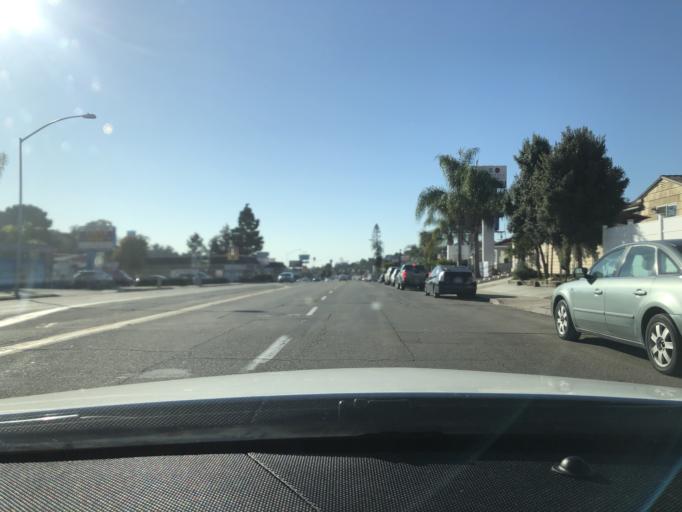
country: US
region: California
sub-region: San Diego County
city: Lemon Grove
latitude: 32.7546
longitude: -117.0589
